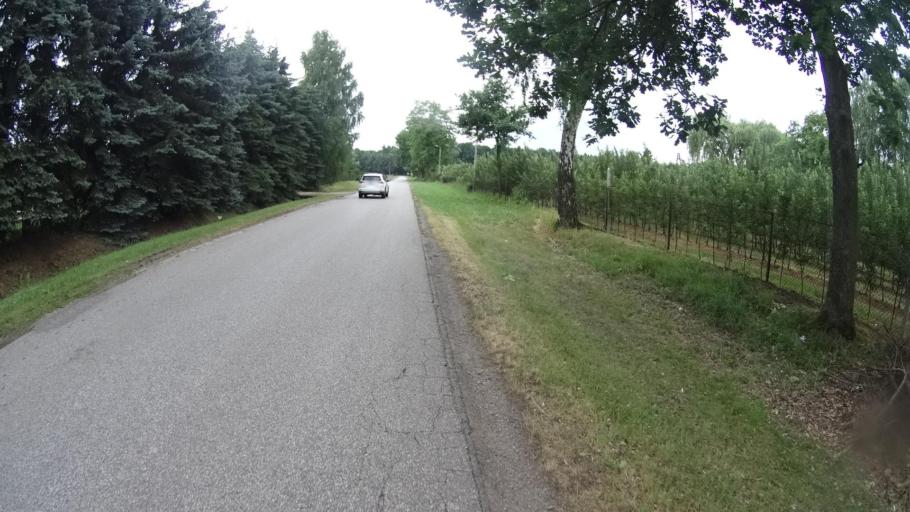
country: PL
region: Masovian Voivodeship
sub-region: Powiat grojecki
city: Goszczyn
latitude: 51.7853
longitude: 20.8551
